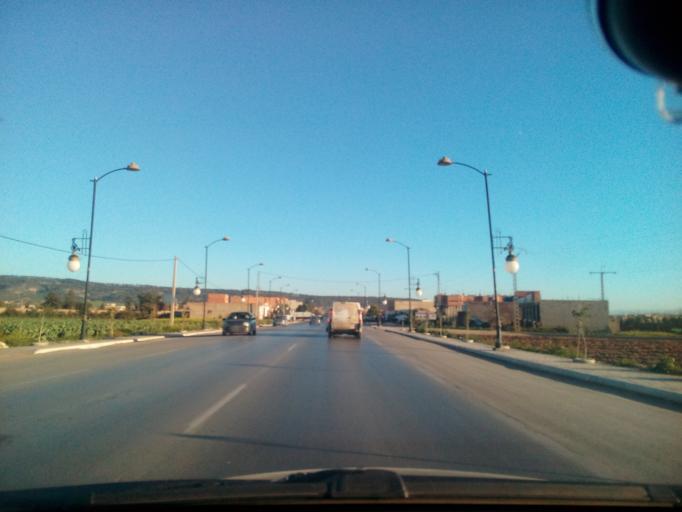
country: DZ
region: Mostaganem
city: Mostaganem
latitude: 35.7848
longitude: 0.1796
